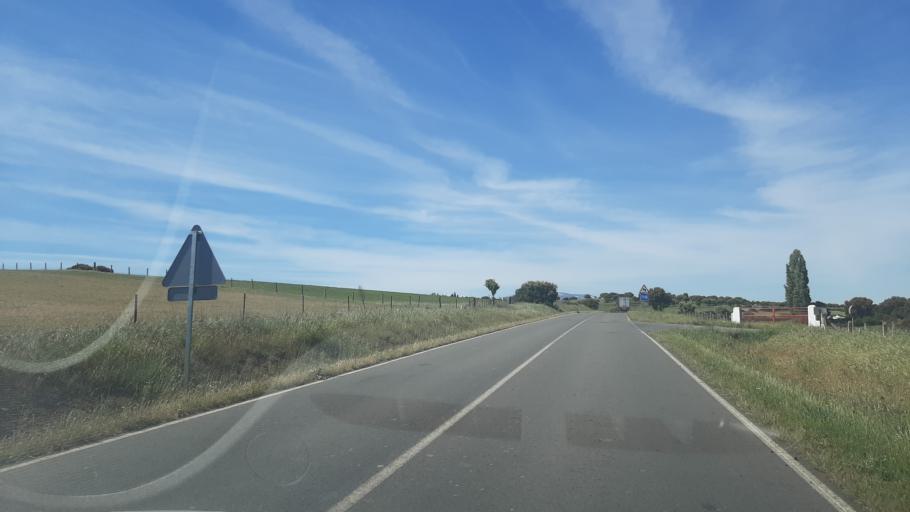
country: ES
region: Castille and Leon
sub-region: Provincia de Salamanca
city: Salvatierra de Tormes
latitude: 40.5514
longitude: -5.5931
